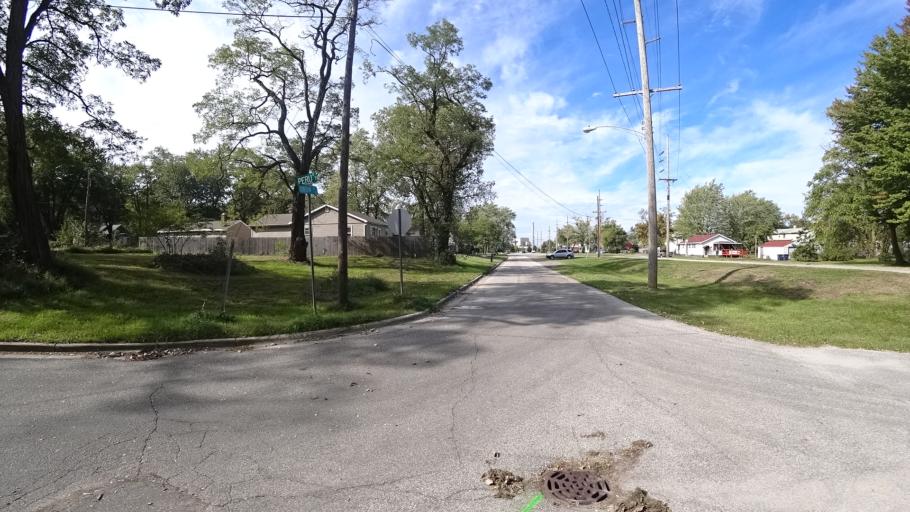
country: US
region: Indiana
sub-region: LaPorte County
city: Michigan City
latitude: 41.7206
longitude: -86.8865
